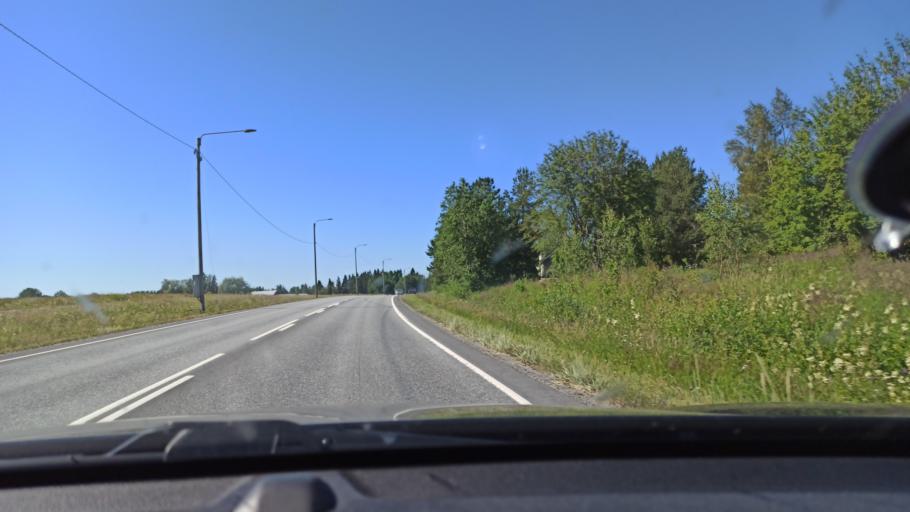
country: FI
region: Ostrobothnia
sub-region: Jakobstadsregionen
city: Bennaes
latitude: 63.6094
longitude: 22.7710
